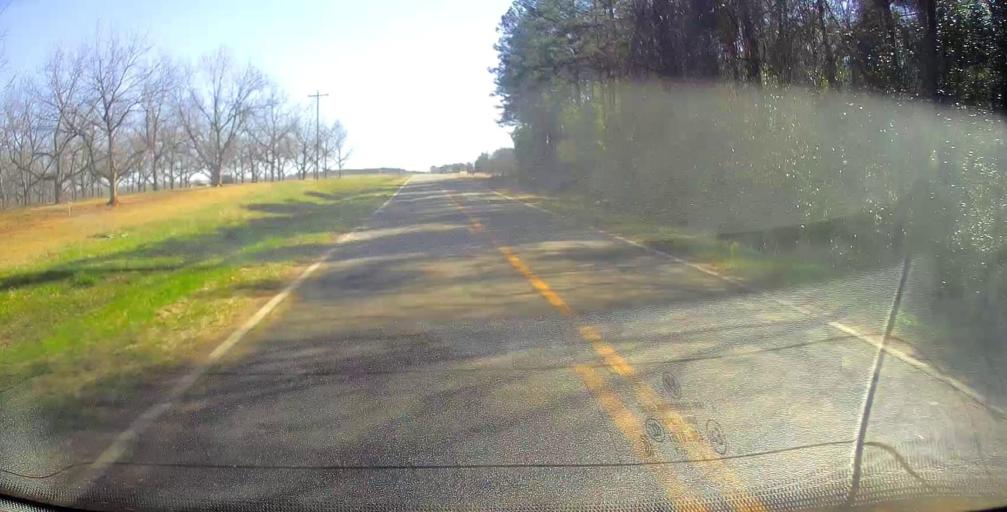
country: US
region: Georgia
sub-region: Crawford County
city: Knoxville
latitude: 32.6139
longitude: -83.9844
